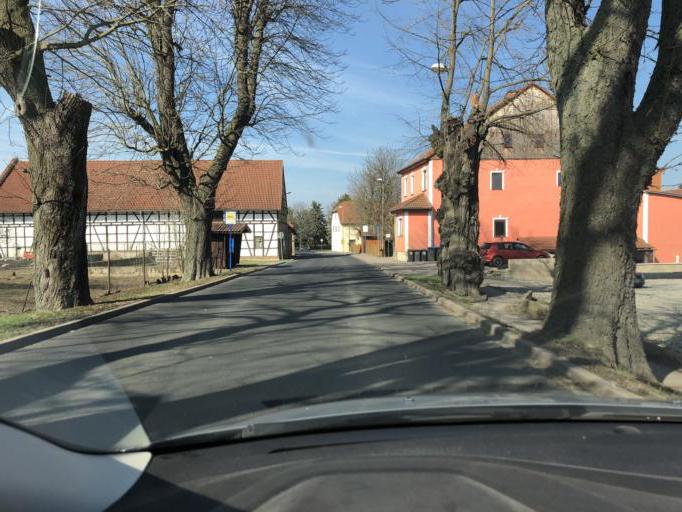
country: DE
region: Thuringia
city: Schwarza
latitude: 50.8274
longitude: 11.3431
